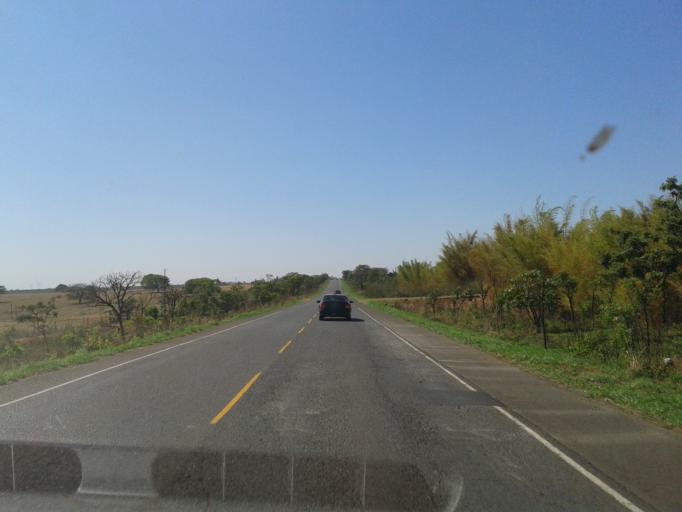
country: BR
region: Minas Gerais
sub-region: Uberlandia
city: Uberlandia
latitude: -19.0396
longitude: -48.0590
